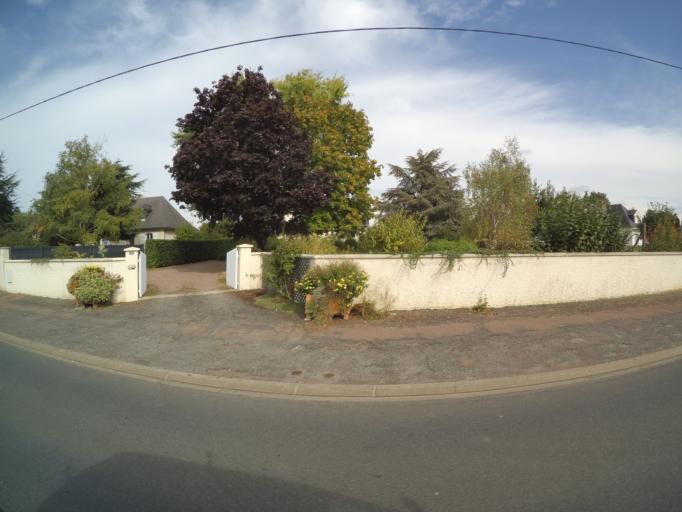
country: FR
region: Pays de la Loire
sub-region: Departement de Maine-et-Loire
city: Doue-la-Fontaine
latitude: 47.1940
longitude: -0.2953
